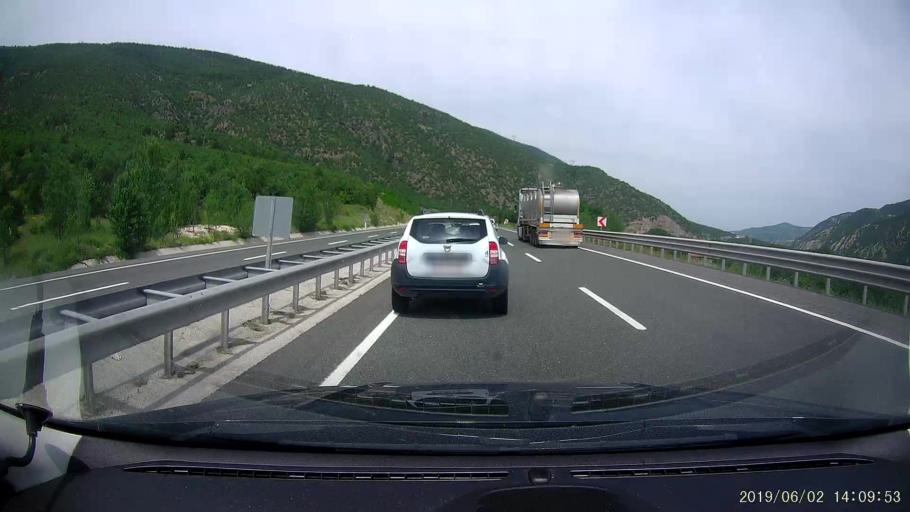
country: TR
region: Cankiri
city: Ilgaz
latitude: 40.8985
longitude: 33.7498
